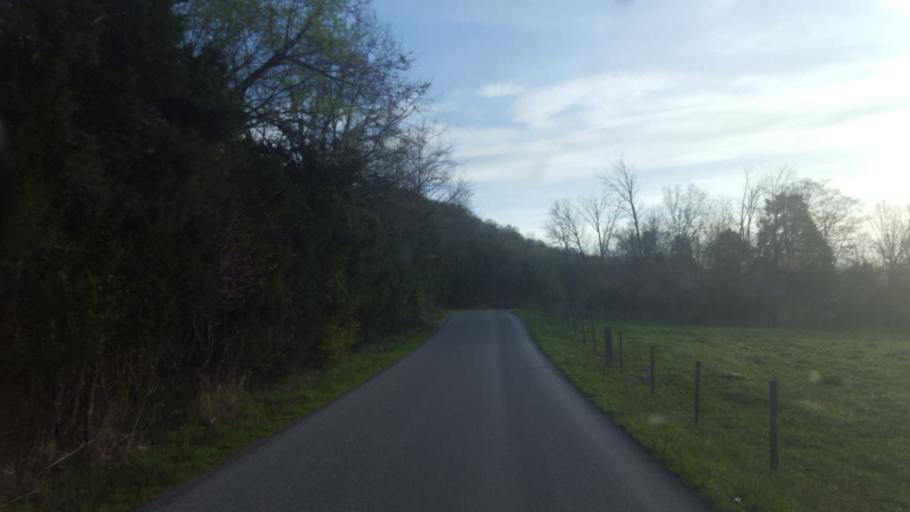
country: US
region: Kentucky
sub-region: Hart County
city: Horse Cave
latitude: 37.2257
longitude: -85.9419
